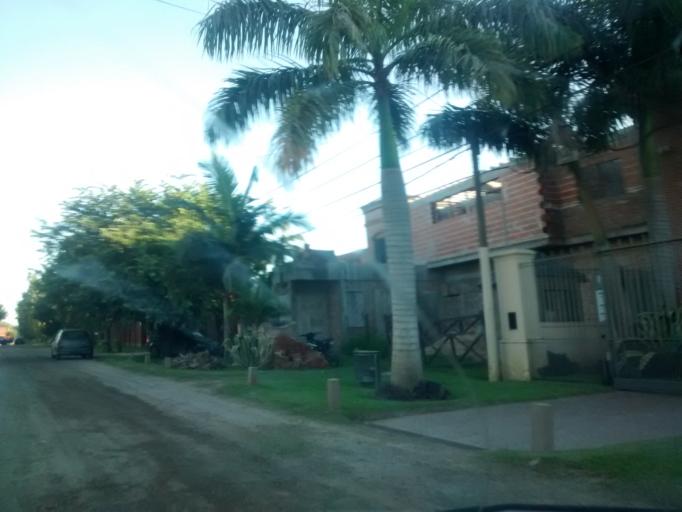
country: AR
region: Chaco
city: Resistencia
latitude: -27.4378
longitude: -58.9677
